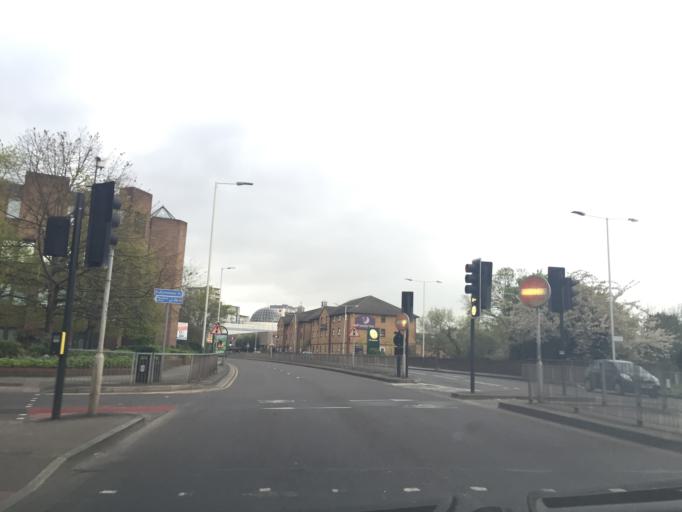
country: GB
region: England
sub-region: Greater London
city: Romford
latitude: 51.5763
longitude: 0.1870
